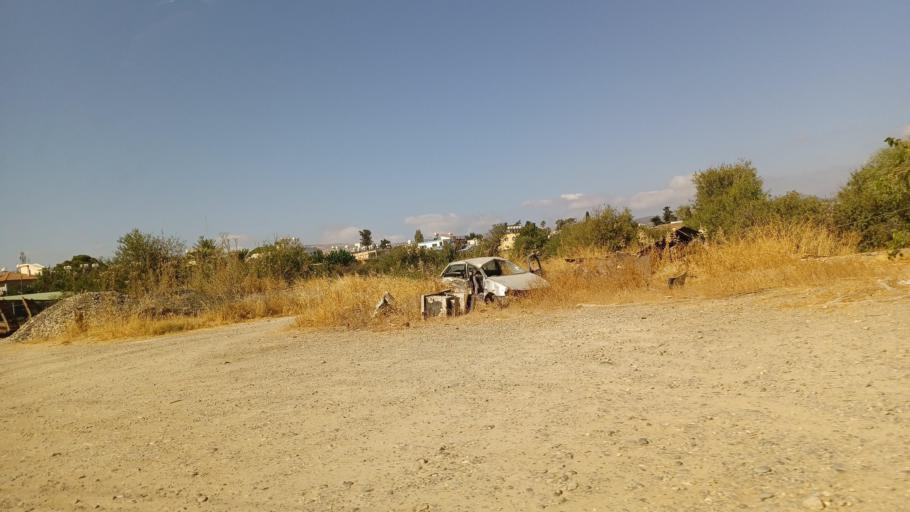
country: CY
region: Pafos
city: Polis
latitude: 35.0387
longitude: 32.4275
